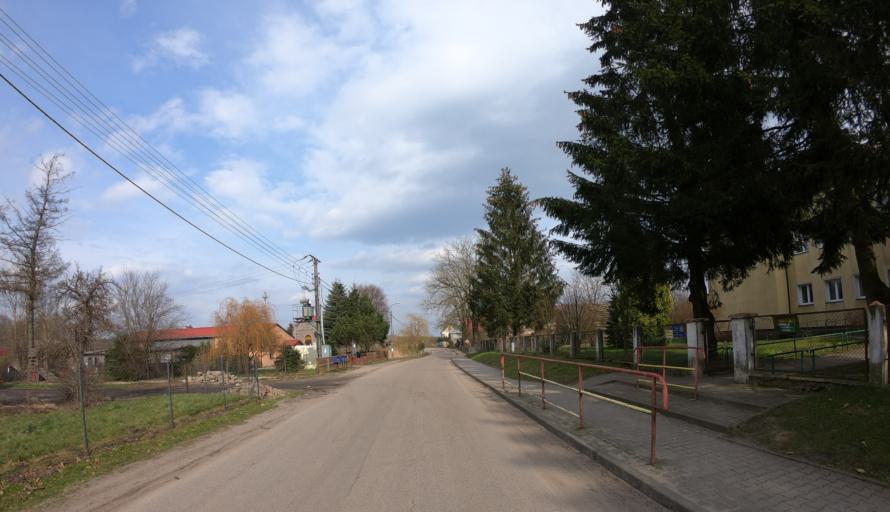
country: PL
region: West Pomeranian Voivodeship
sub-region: Powiat swidwinski
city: Swidwin
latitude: 53.8379
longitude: 15.8440
